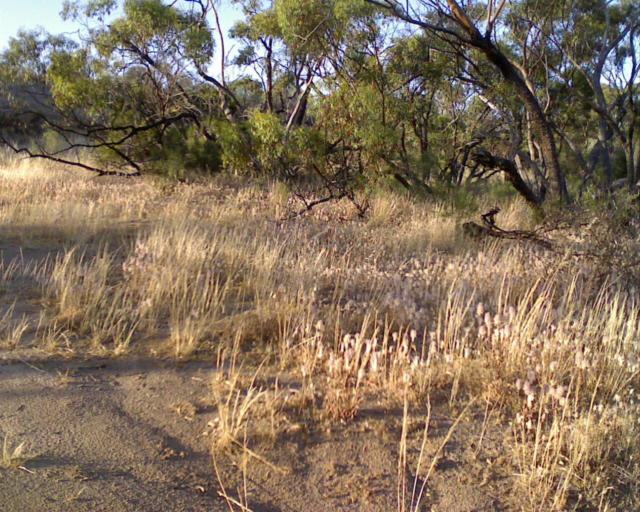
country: AU
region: Western Australia
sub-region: Merredin
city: Merredin
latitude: -30.8369
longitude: 117.9016
